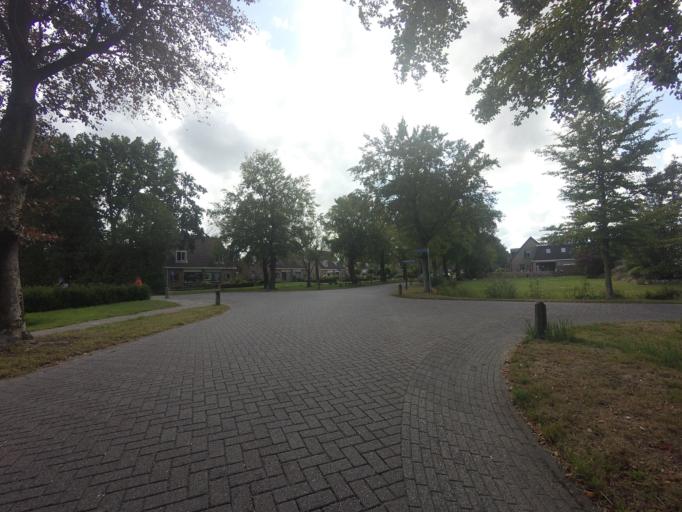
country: NL
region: Drenthe
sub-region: Gemeente Westerveld
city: Dwingeloo
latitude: 52.9564
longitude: 6.3408
